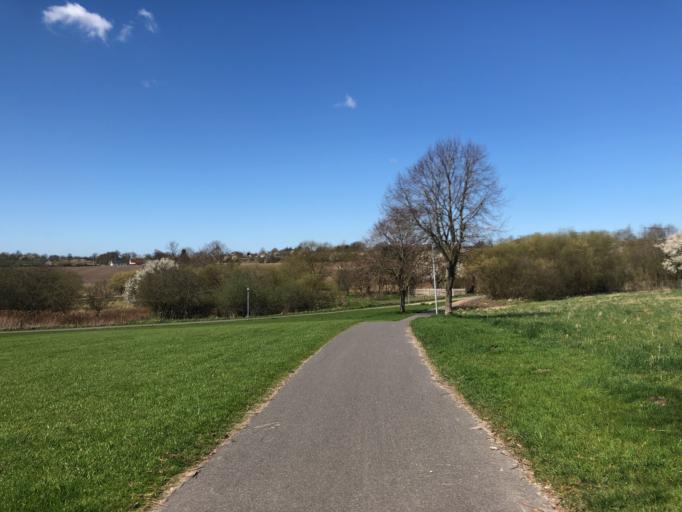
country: DK
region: Zealand
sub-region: Ringsted Kommune
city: Ringsted
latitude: 55.4348
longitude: 11.7802
